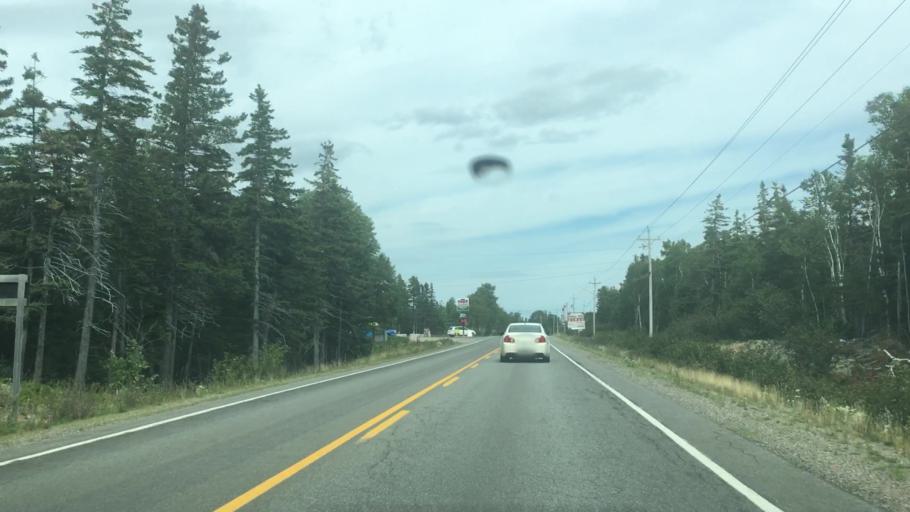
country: CA
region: Nova Scotia
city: Sydney Mines
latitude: 46.5150
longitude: -60.4281
